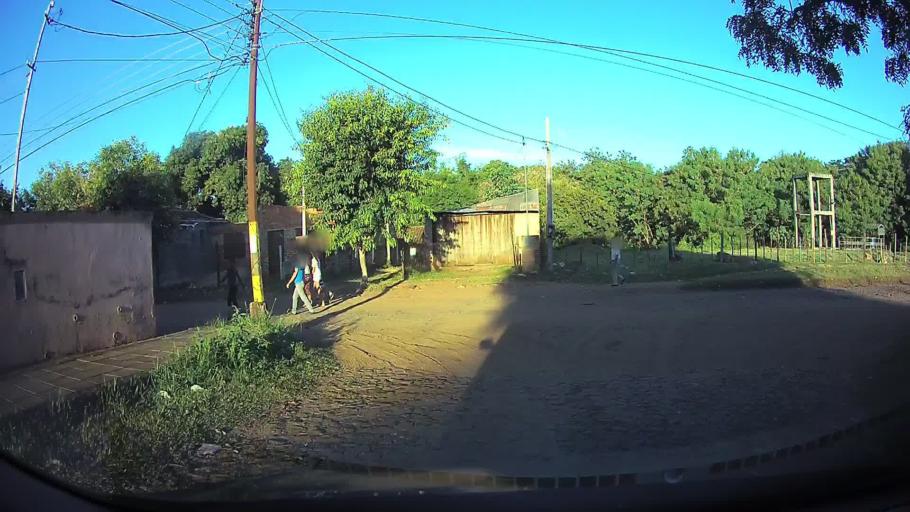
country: PY
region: Central
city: San Lorenzo
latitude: -25.2629
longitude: -57.4873
